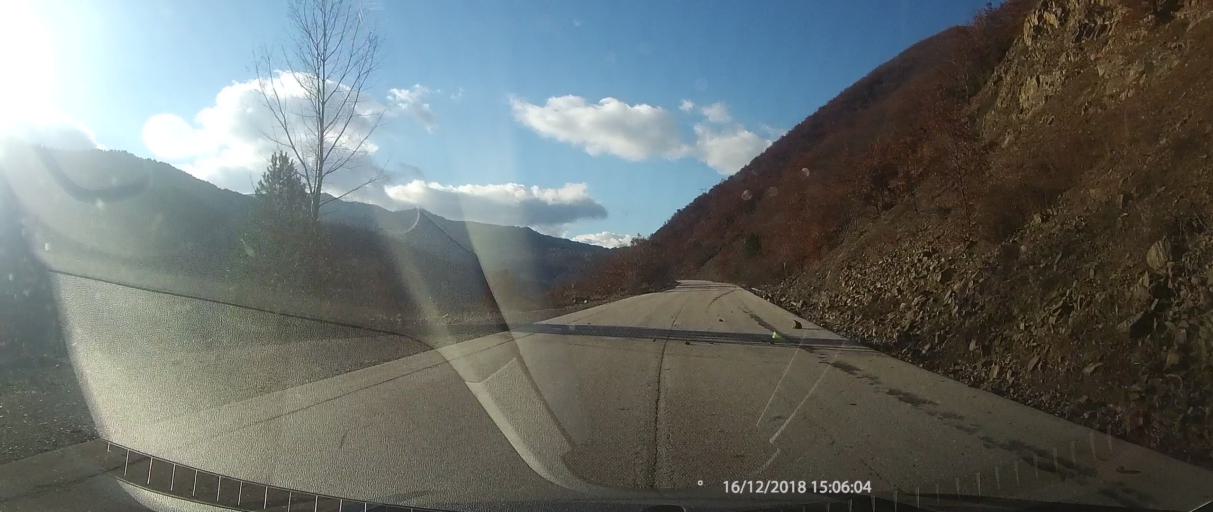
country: GR
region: West Macedonia
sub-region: Nomos Kastorias
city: Nestorio
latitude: 40.2203
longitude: 20.9492
